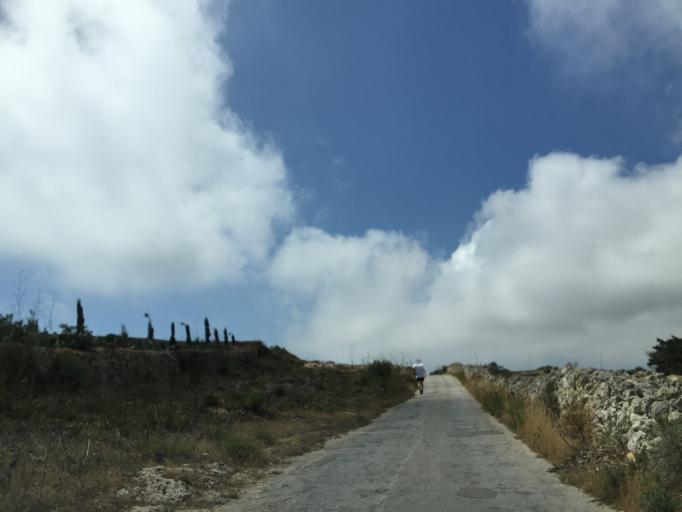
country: MT
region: Dingli
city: Dingli
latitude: 35.8633
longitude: 14.3667
